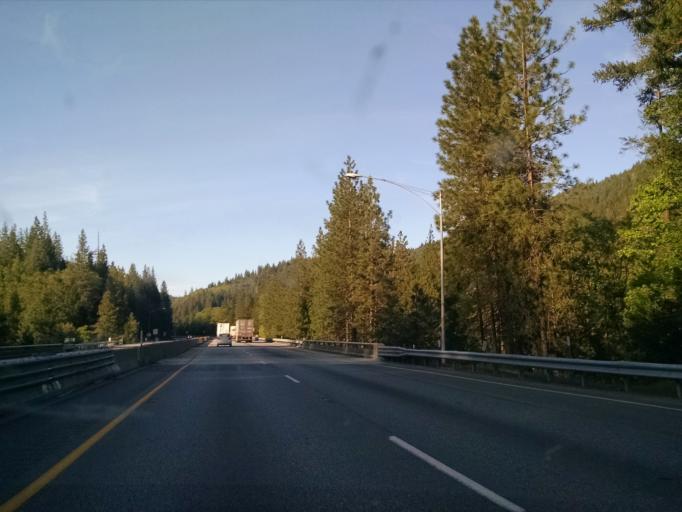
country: US
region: California
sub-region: Siskiyou County
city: Dunsmuir
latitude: 41.0714
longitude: -122.3584
